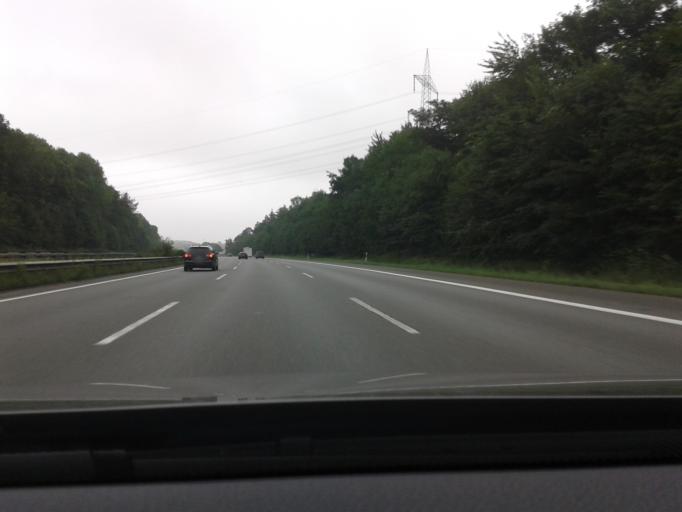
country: DE
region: North Rhine-Westphalia
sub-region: Regierungsbezirk Detmold
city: Leopoldshohe
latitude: 52.0432
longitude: 8.6512
